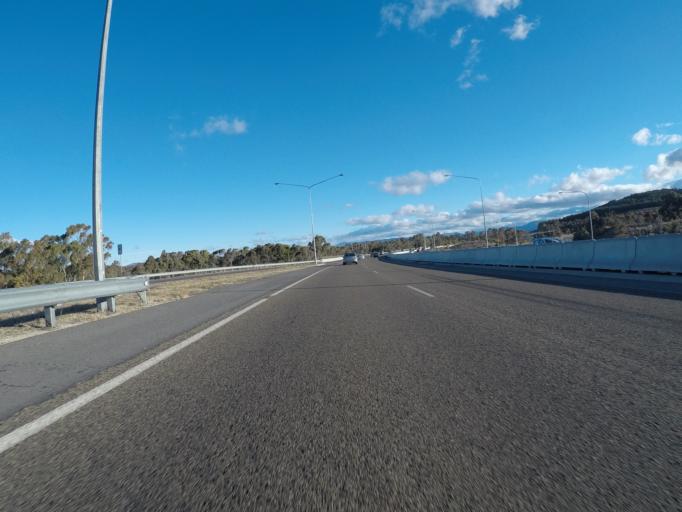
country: AU
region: Australian Capital Territory
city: Acton
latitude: -35.2832
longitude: 149.0857
